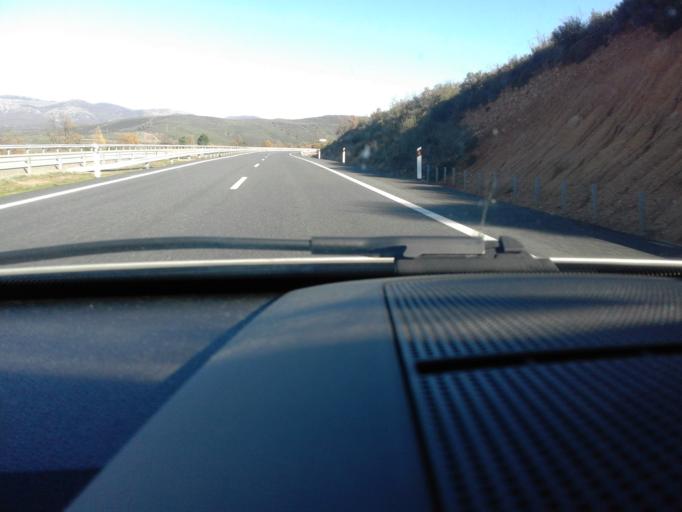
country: ES
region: Castille and Leon
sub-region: Provincia de Leon
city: Santa Maria de Ordas
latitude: 42.7363
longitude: -5.7811
